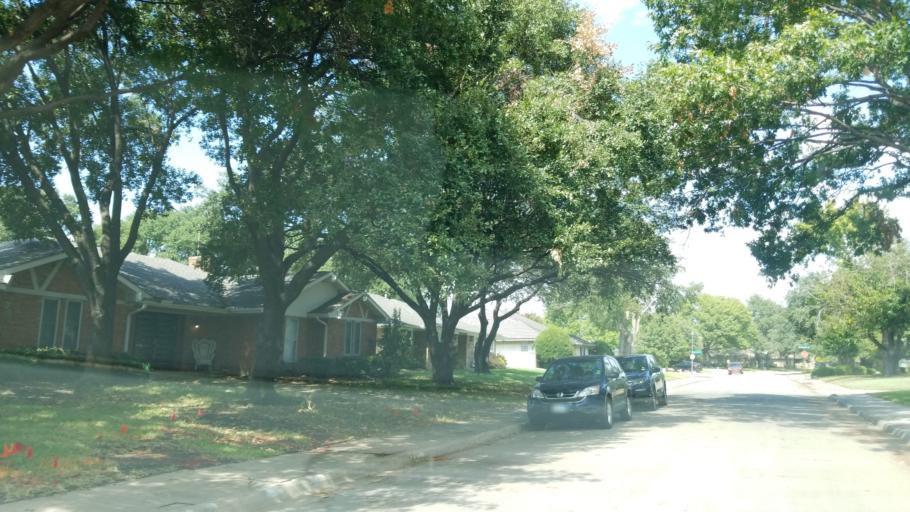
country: US
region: Texas
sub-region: Dallas County
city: Addison
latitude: 32.9661
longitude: -96.7856
